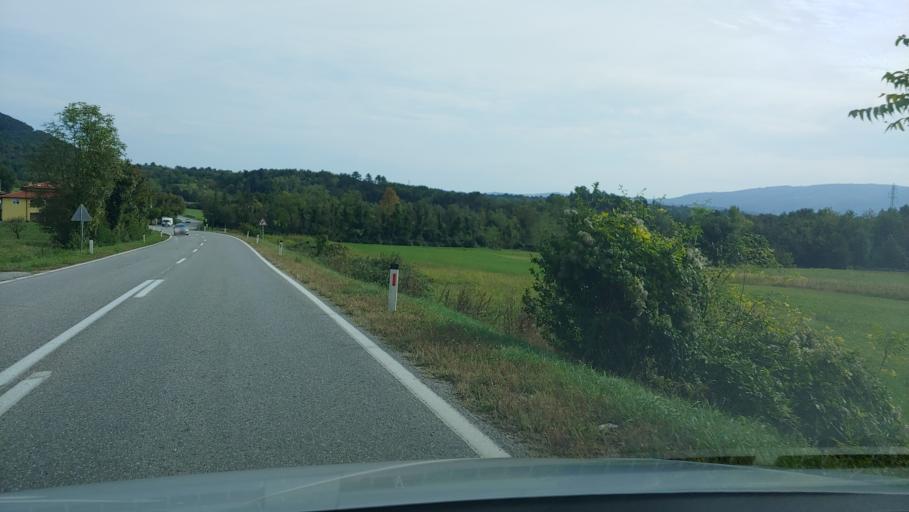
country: SI
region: Nova Gorica
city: Sempas
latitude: 45.9210
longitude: 13.7560
